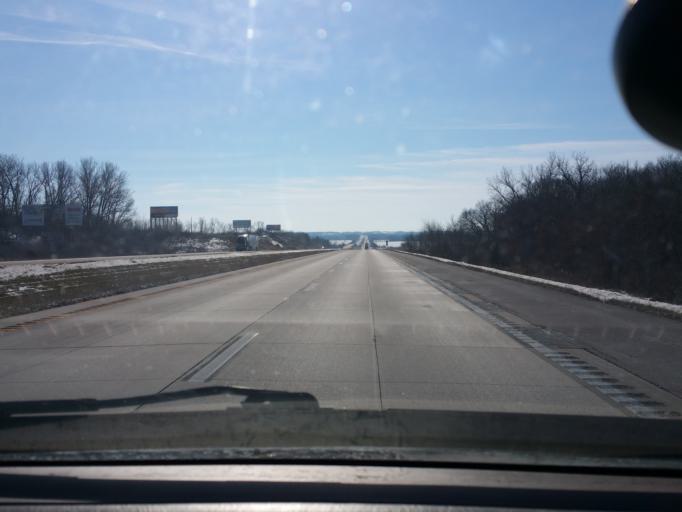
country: US
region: Missouri
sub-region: Daviess County
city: Gallatin
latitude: 40.0609
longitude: -94.0942
